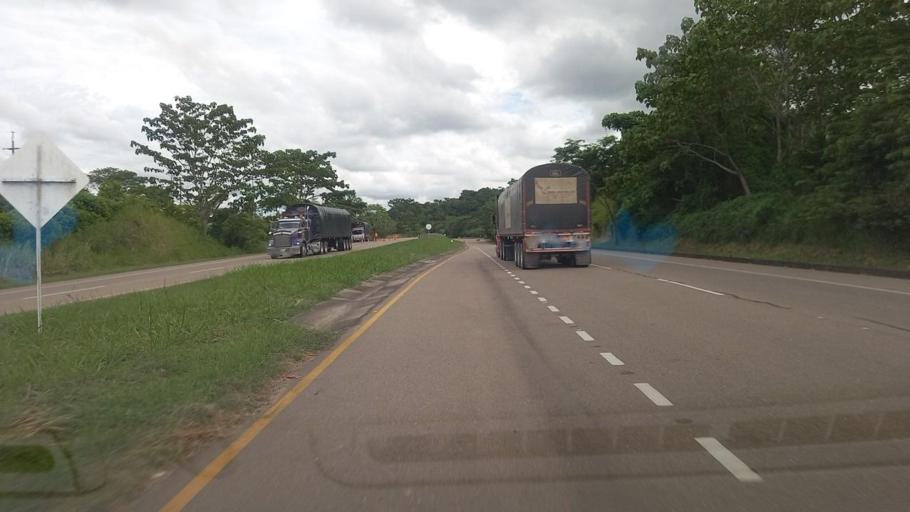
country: CO
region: Boyaca
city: Puerto Boyaca
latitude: 6.1539
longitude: -74.5729
